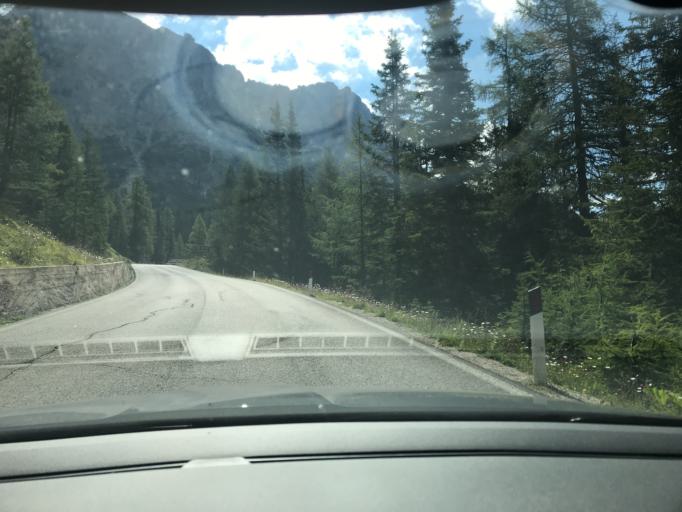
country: IT
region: Veneto
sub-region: Provincia di Belluno
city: Livinallongo del Col di Lana
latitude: 46.5416
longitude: 11.9792
